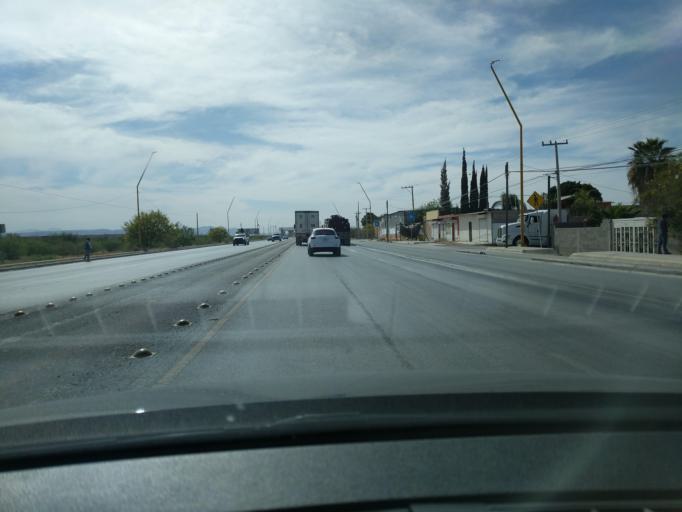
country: MX
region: Coahuila
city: Matamoros
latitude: 25.5359
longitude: -103.2578
